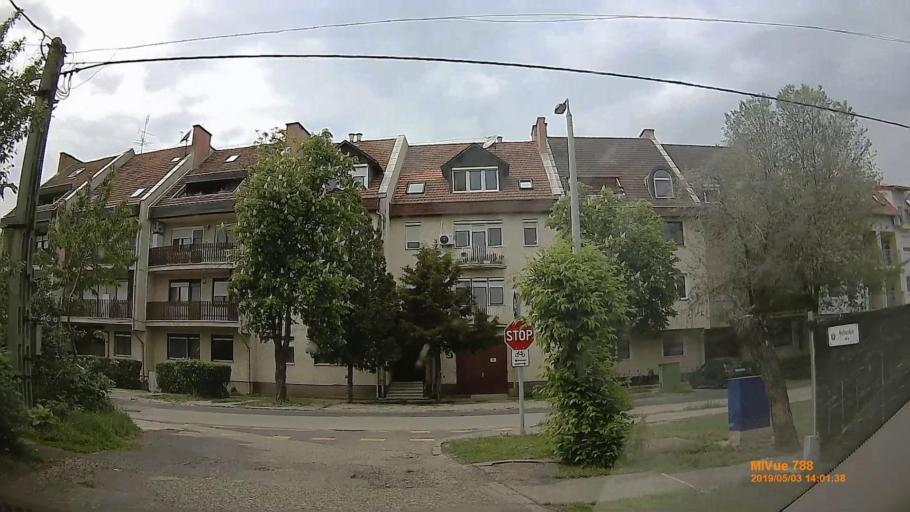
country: HU
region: Jasz-Nagykun-Szolnok
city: Szolnok
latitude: 47.1852
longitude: 20.1918
